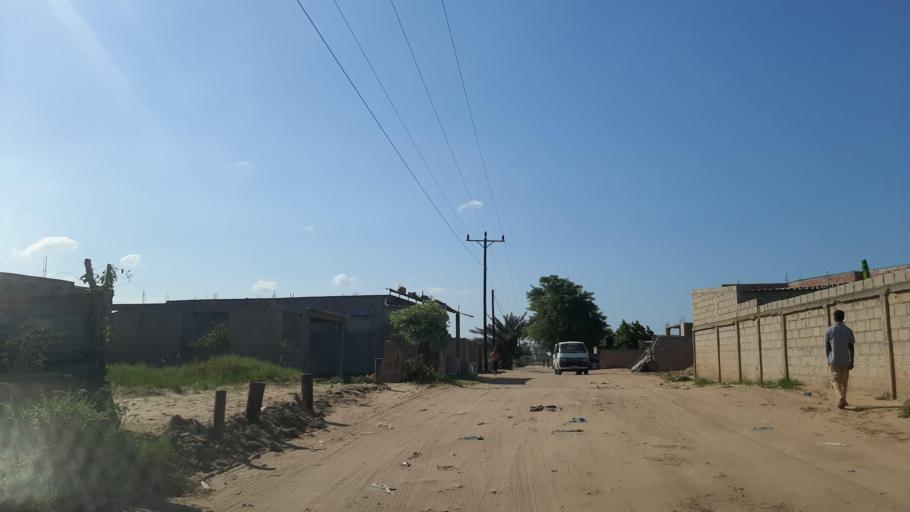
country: MZ
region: Maputo
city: Matola
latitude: -25.8073
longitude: 32.4915
